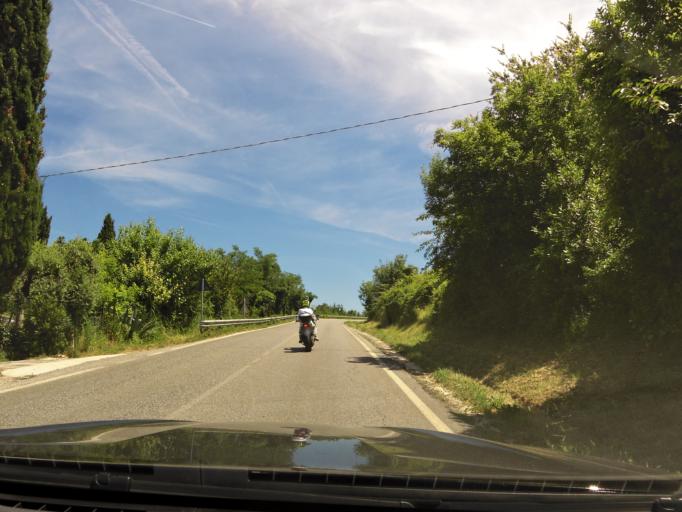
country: IT
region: The Marches
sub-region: Provincia di Ancona
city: Pietra la Croce
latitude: 43.6036
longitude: 13.5417
